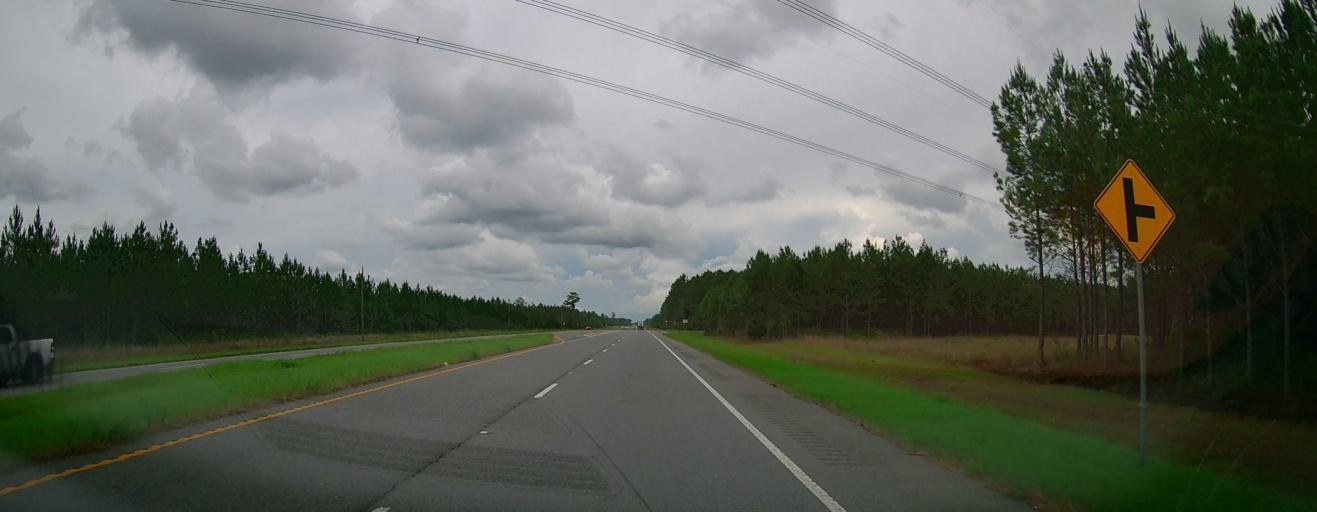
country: US
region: Georgia
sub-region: Wayne County
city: Jesup
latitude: 31.6790
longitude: -82.0857
